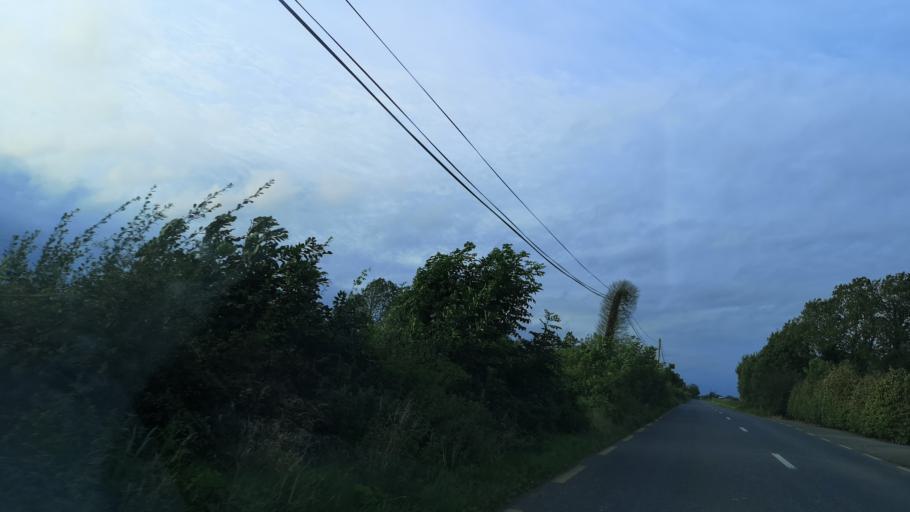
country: IE
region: Leinster
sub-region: Uibh Fhaili
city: Ferbane
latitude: 53.3193
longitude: -7.8214
